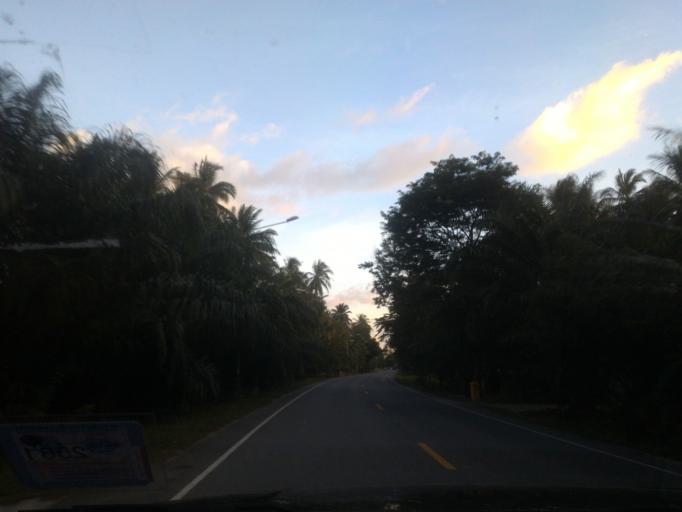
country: TH
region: Nakhon Si Thammarat
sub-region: Amphoe Nopphitam
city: Nopphitam
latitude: 9.0362
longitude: 99.9041
